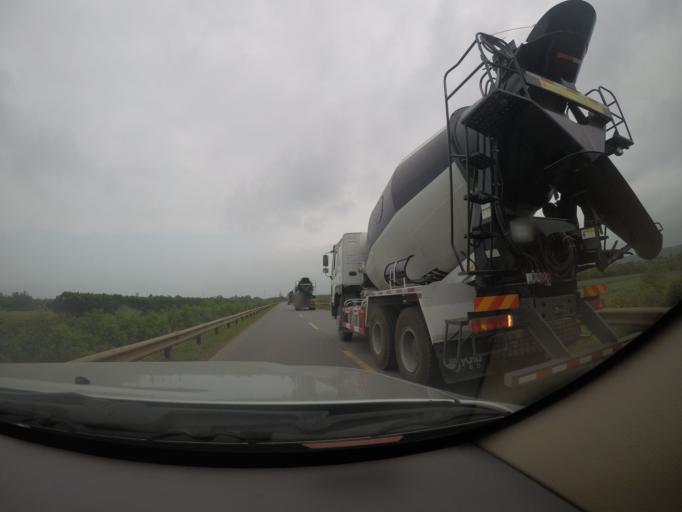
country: VN
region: Quang Binh
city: Kien Giang
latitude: 17.2524
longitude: 106.6786
